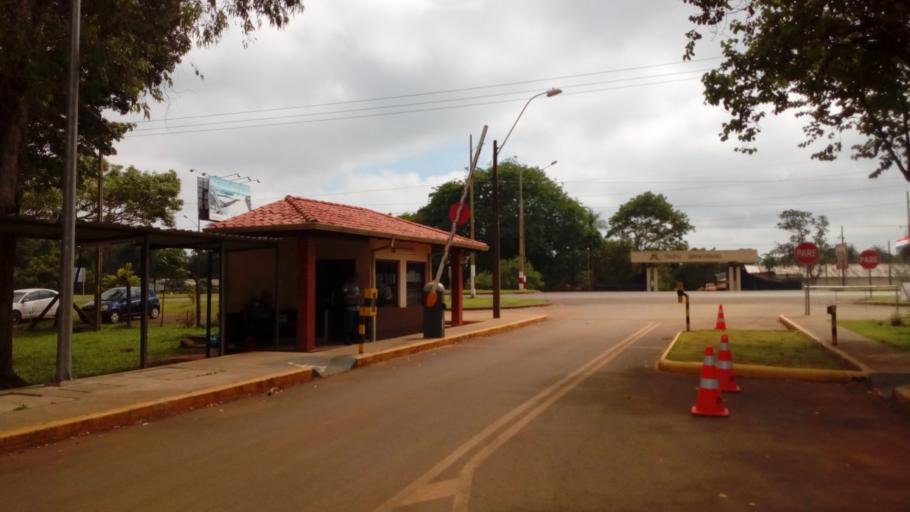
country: PY
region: Alto Parana
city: Ciudad del Este
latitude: -25.4415
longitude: -54.6348
